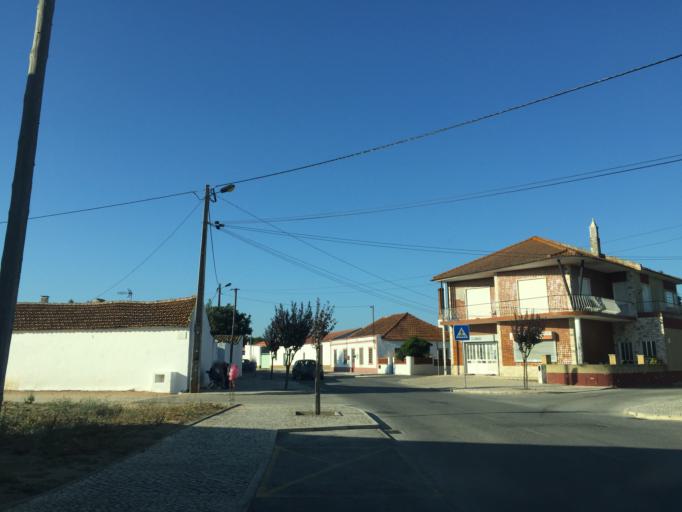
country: PT
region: Lisbon
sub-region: Azambuja
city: Aveiras de Cima
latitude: 39.1370
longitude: -8.9227
